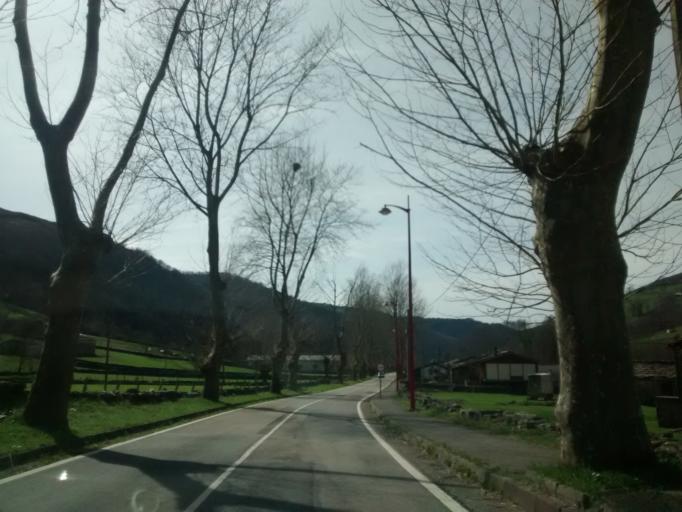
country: ES
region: Cantabria
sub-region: Provincia de Cantabria
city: Vega de Pas
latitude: 43.1572
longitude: -3.7933
